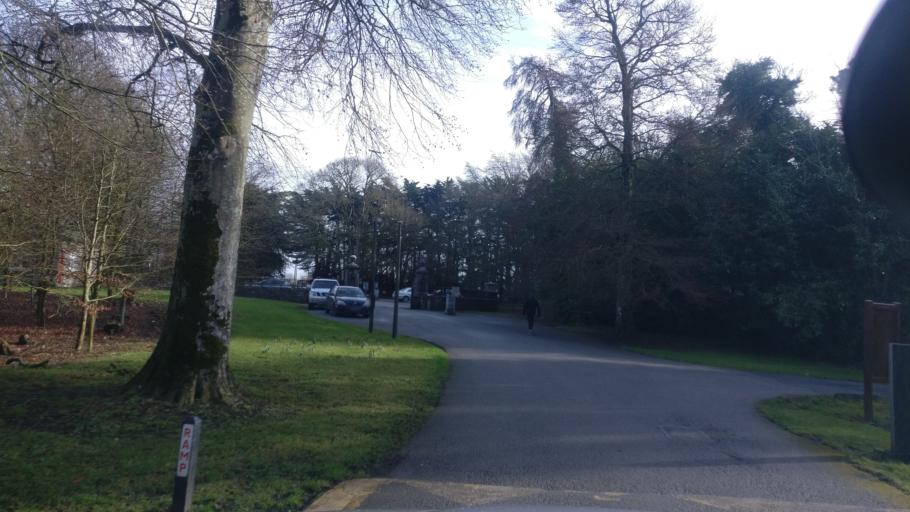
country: IE
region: Leinster
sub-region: Kilkenny
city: Thomastown
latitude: 52.5284
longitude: -7.1698
